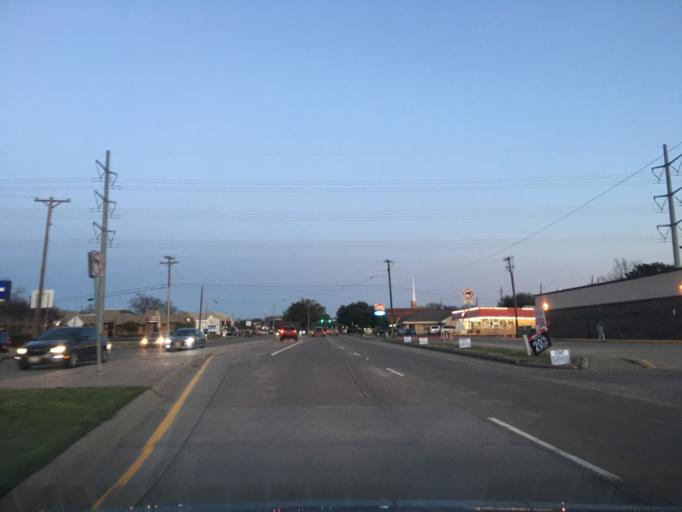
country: US
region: Texas
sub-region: Collin County
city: McKinney
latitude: 33.1983
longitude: -96.6375
